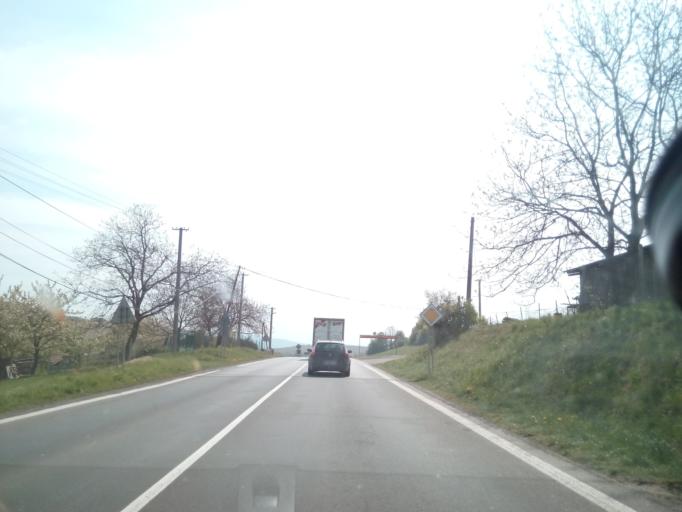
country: SK
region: Presovsky
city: Giraltovce
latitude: 49.0362
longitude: 21.4603
